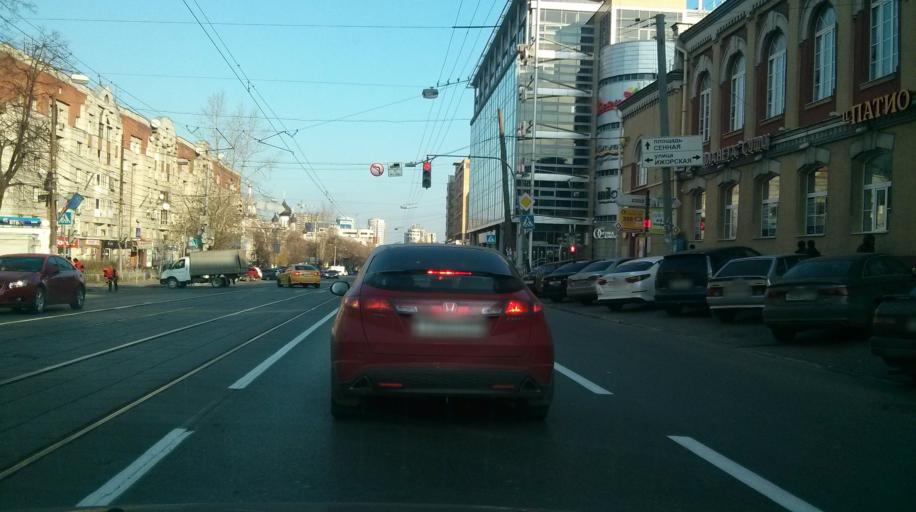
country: RU
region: Nizjnij Novgorod
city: Nizhniy Novgorod
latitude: 56.3168
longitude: 44.0186
